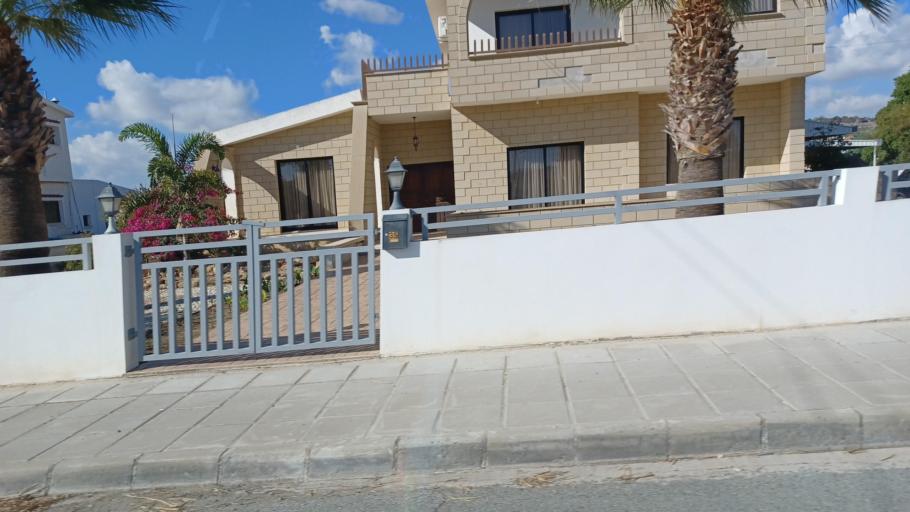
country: CY
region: Larnaka
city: Pyla
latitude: 34.9966
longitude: 33.6852
